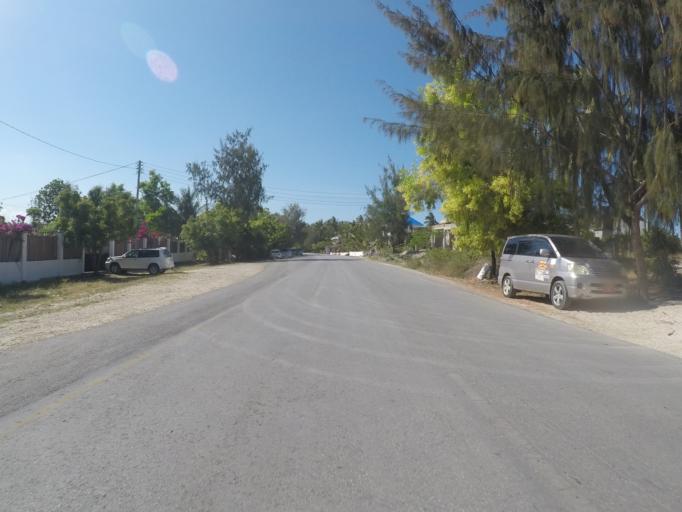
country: TZ
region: Zanzibar Central/South
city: Nganane
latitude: -6.2701
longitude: 39.5326
